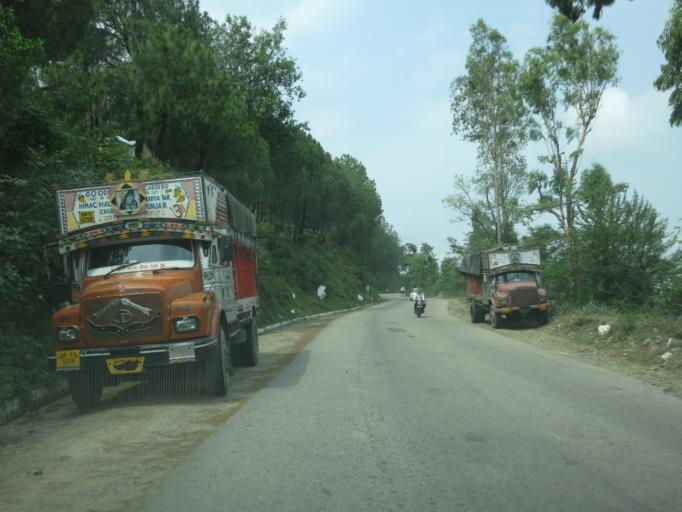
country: IN
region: Himachal Pradesh
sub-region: Bilaspur
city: Bilaspur
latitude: 31.2604
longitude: 76.8693
